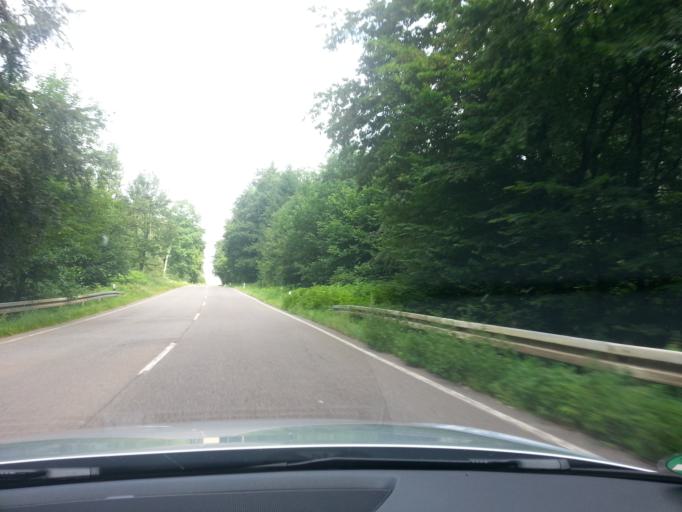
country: DE
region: Saarland
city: Weiten
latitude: 49.5160
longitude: 6.5616
